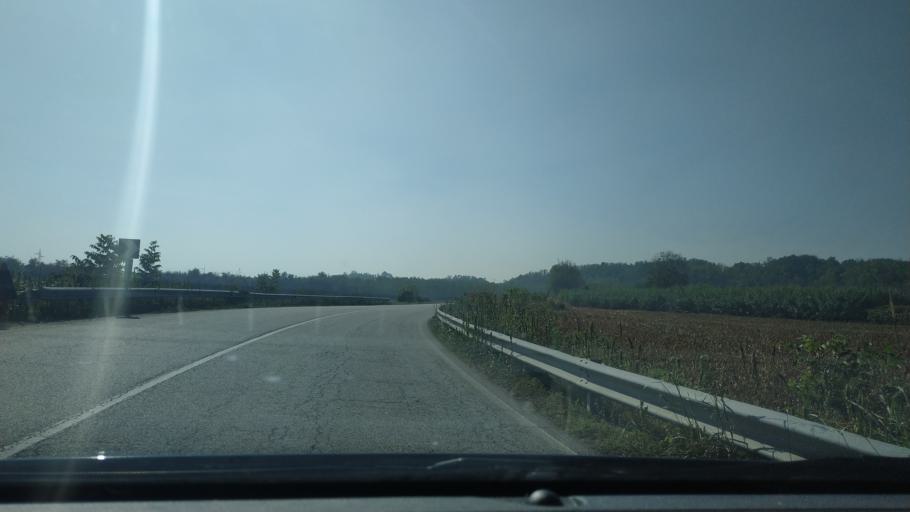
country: IT
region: Piedmont
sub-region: Provincia di Alessandria
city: Bozzole
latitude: 45.0507
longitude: 8.6194
